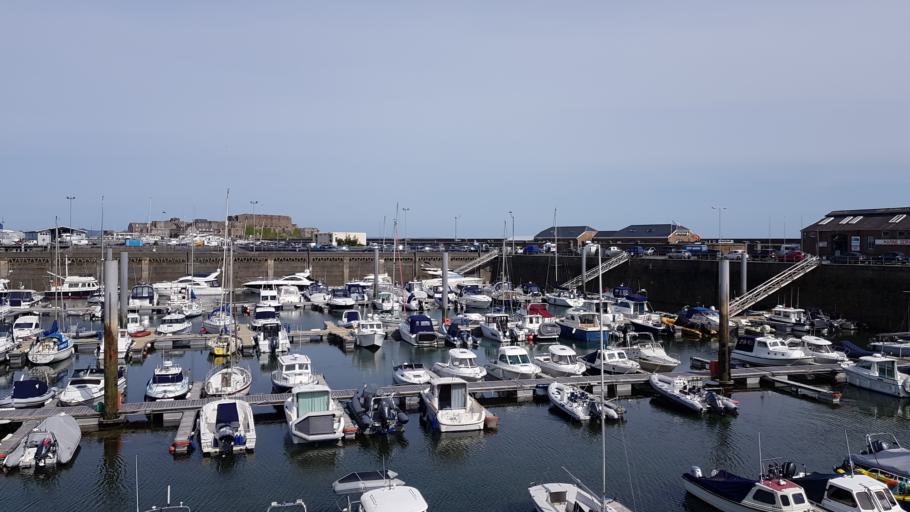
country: GG
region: St Peter Port
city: Saint Peter Port
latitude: 49.4534
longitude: -2.5352
